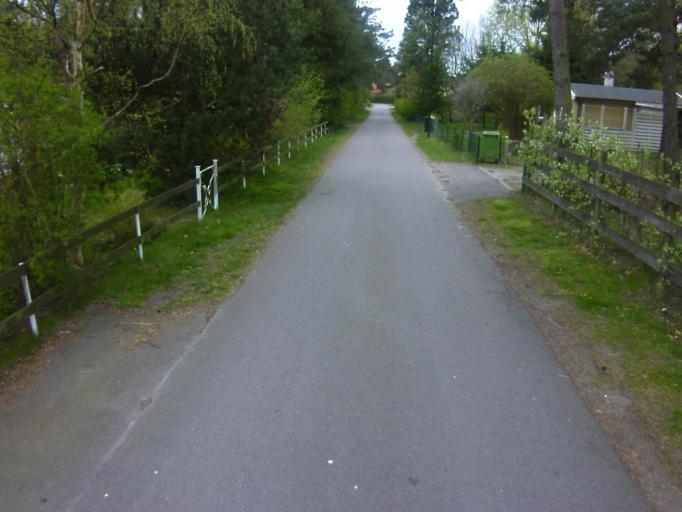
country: SE
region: Skane
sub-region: Kavlinge Kommun
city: Hofterup
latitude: 55.7641
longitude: 12.9819
